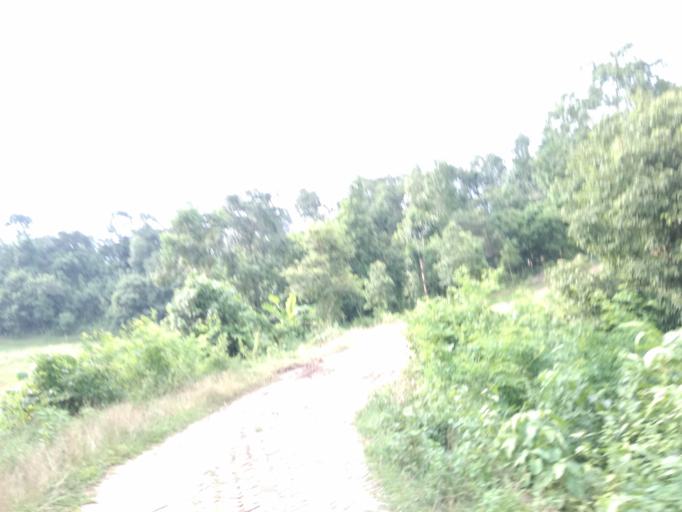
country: BD
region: Chittagong
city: Manikchari
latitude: 22.9262
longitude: 91.9120
